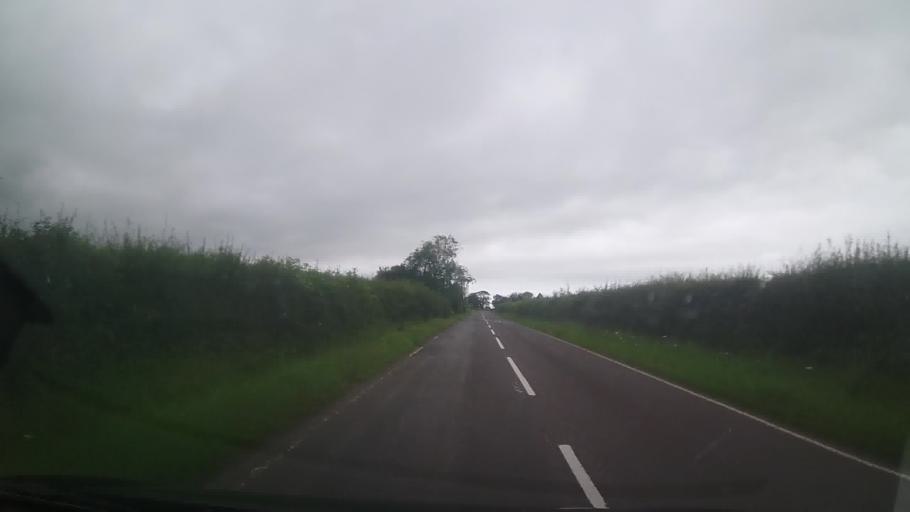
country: GB
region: Wales
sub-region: Gwynedd
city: Caernarfon
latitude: 53.1774
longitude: -4.2848
